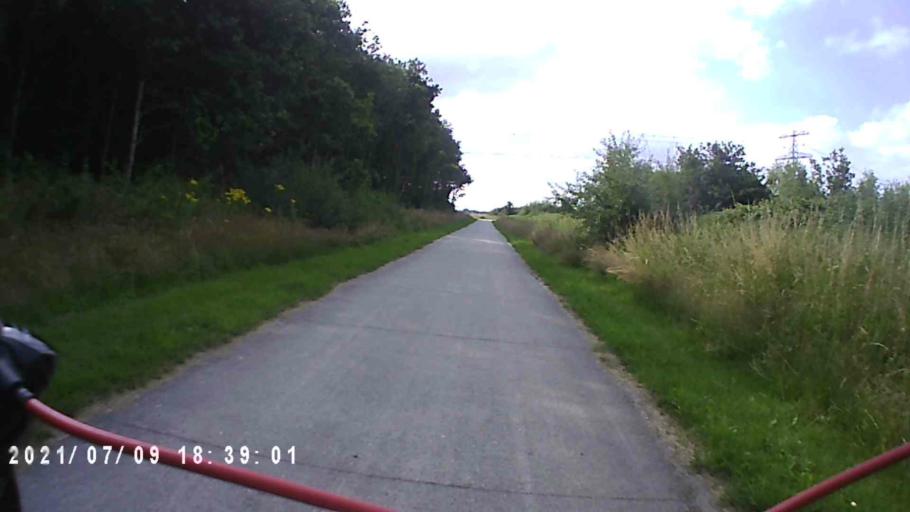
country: NL
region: Groningen
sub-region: Gemeente Pekela
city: Oude Pekela
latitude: 53.0808
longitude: 6.9457
